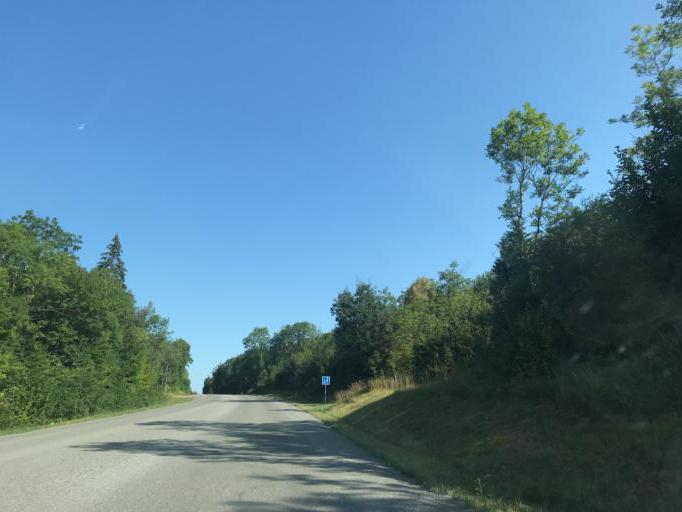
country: FR
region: Franche-Comte
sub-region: Departement du Jura
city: Lavans-les-Saint-Claude
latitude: 46.3858
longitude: 5.7455
